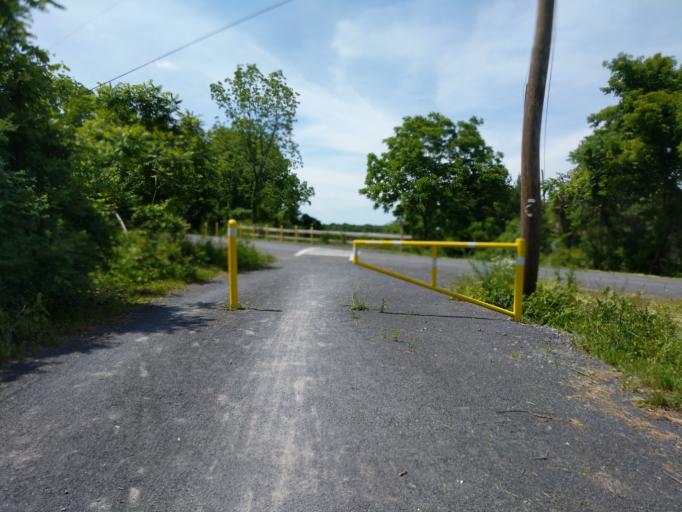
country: US
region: New York
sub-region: Tompkins County
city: Northwest Ithaca
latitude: 42.5124
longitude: -76.5599
